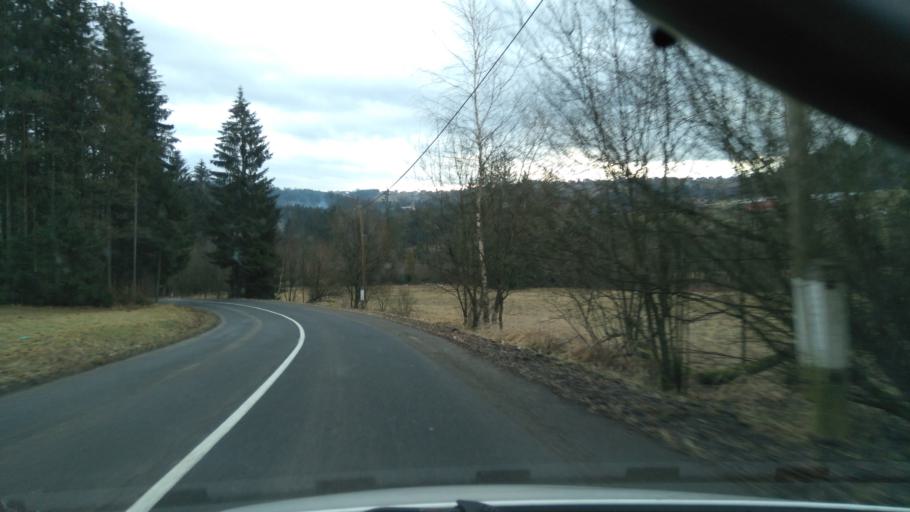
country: CZ
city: Bukovec
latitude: 49.5531
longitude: 18.8468
